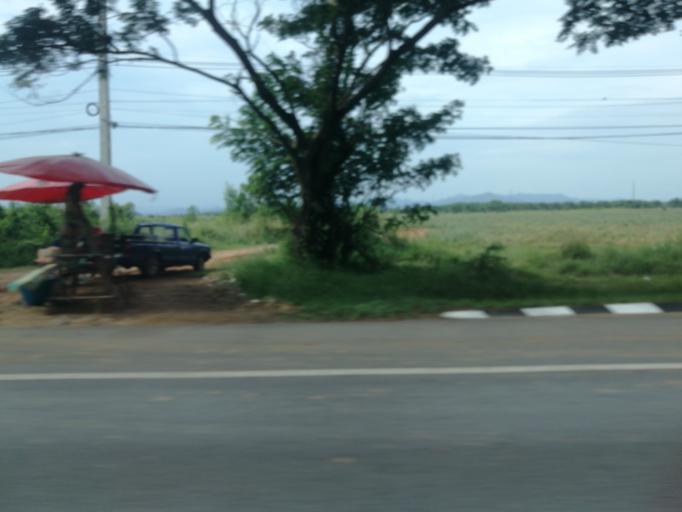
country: TH
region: Prachuap Khiri Khan
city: Hua Hin
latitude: 12.5375
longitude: 99.8766
